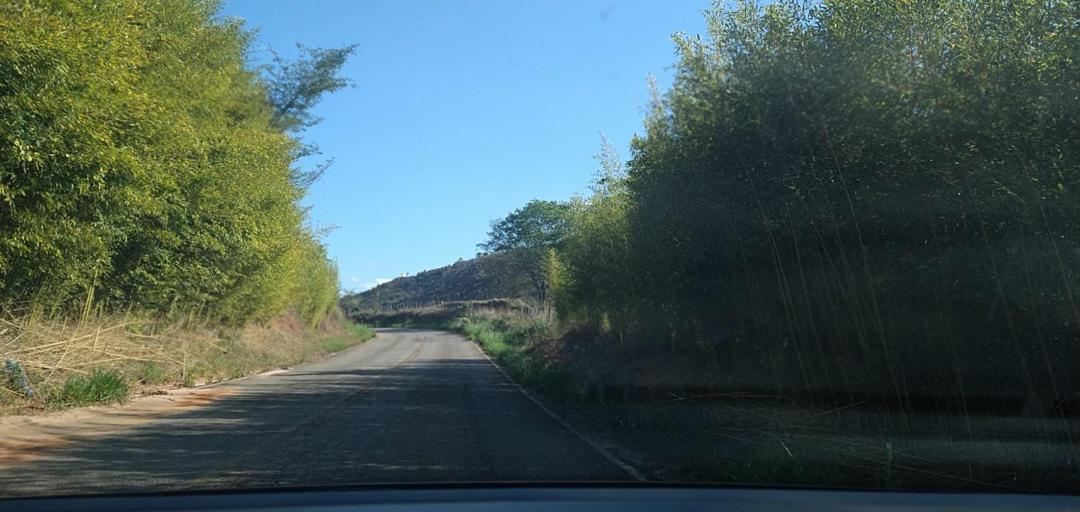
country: BR
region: Minas Gerais
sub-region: Alvinopolis
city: Alvinopolis
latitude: -20.2018
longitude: -42.9284
